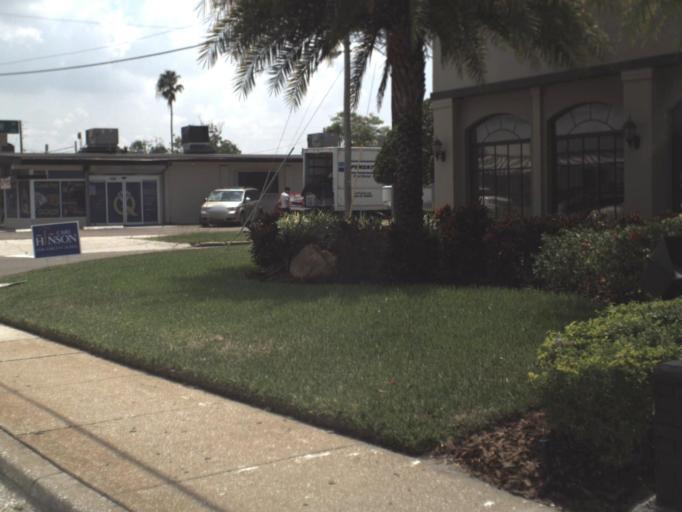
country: US
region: Florida
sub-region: Hillsborough County
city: Tampa
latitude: 27.9447
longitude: -82.4946
